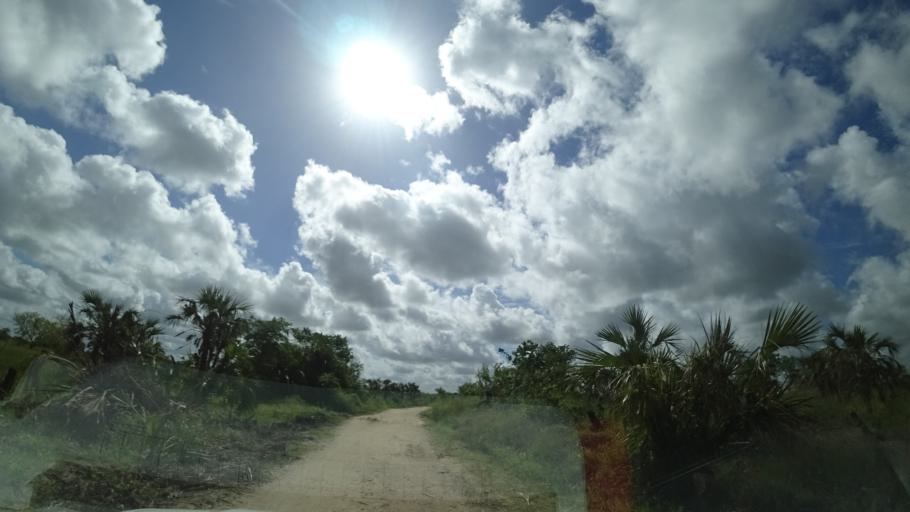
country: MZ
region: Sofala
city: Dondo
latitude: -19.3880
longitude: 34.5796
